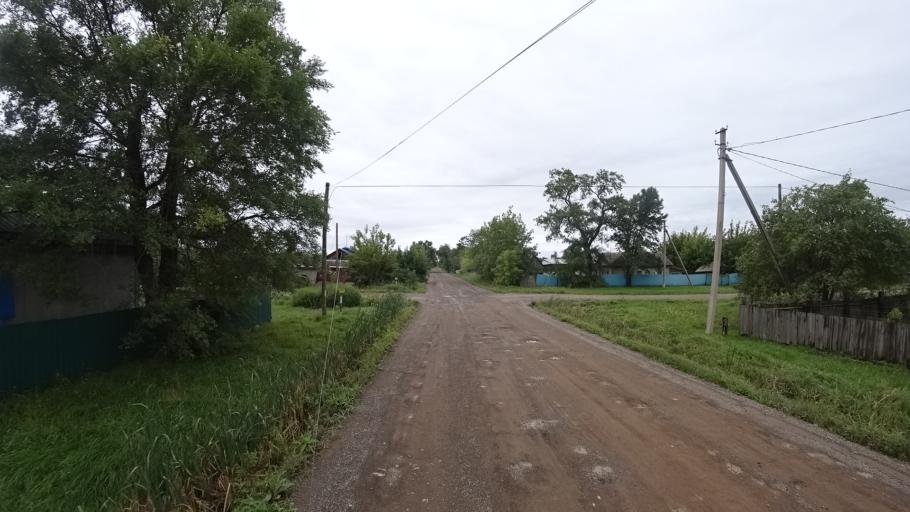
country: RU
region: Primorskiy
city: Chernigovka
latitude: 44.3399
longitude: 132.5677
